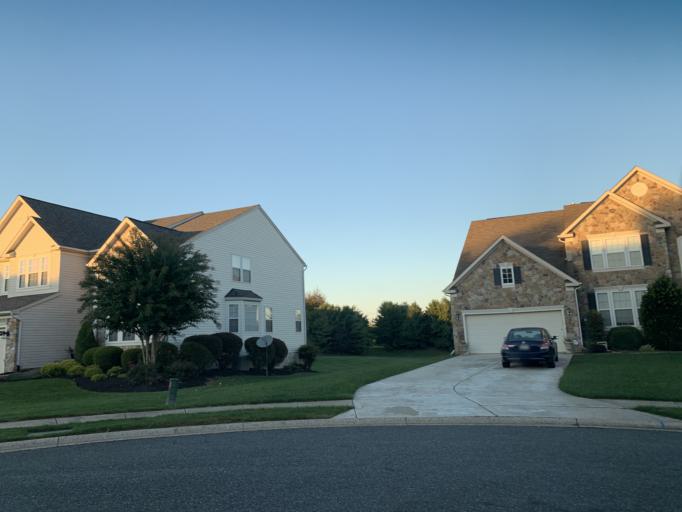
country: US
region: Maryland
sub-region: Harford County
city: Bel Air South
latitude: 39.5275
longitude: -76.2936
